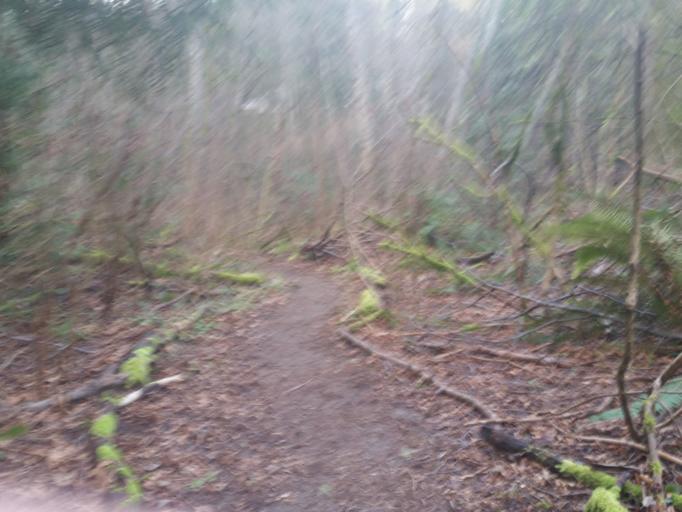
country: US
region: Washington
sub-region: King County
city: Lake Forest Park
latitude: 47.7028
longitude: -122.3096
